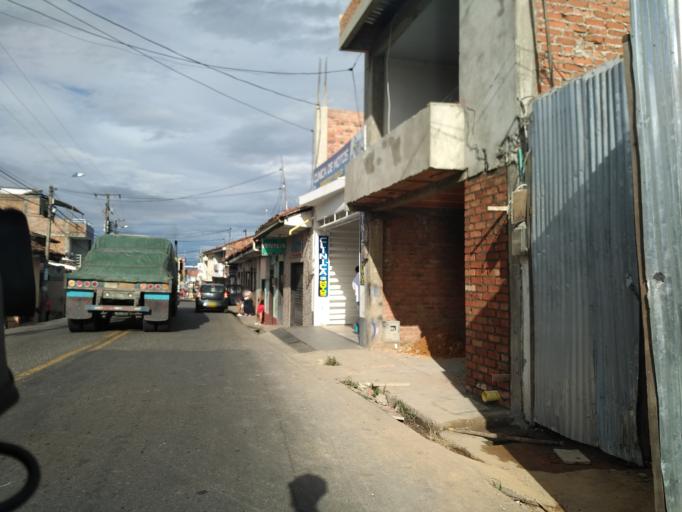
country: CO
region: Cauca
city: El Bordo
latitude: 2.1153
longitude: -76.9859
